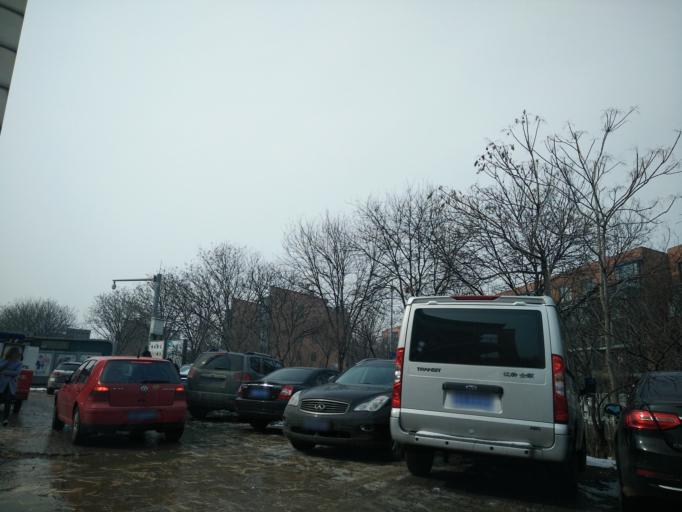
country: CN
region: Beijing
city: Jiugong
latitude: 39.7905
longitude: 116.4928
